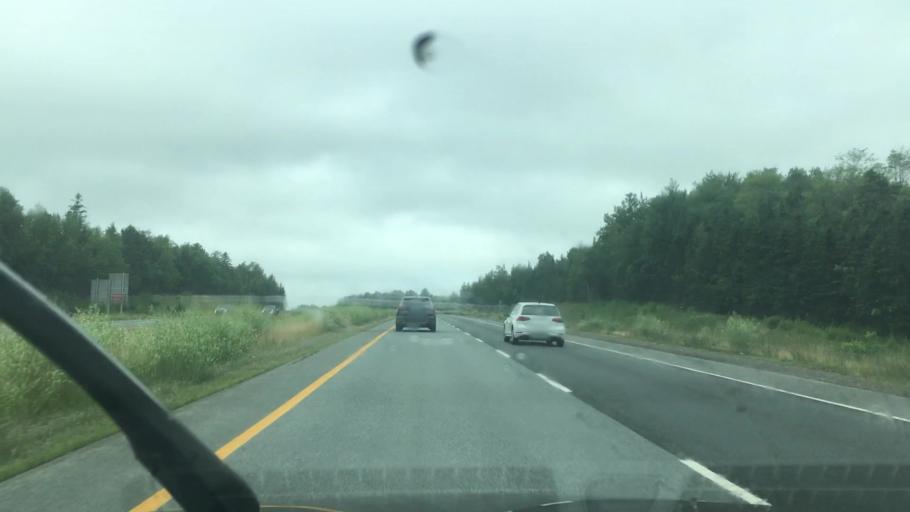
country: CA
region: Nova Scotia
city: Truro
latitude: 45.2655
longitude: -63.2922
